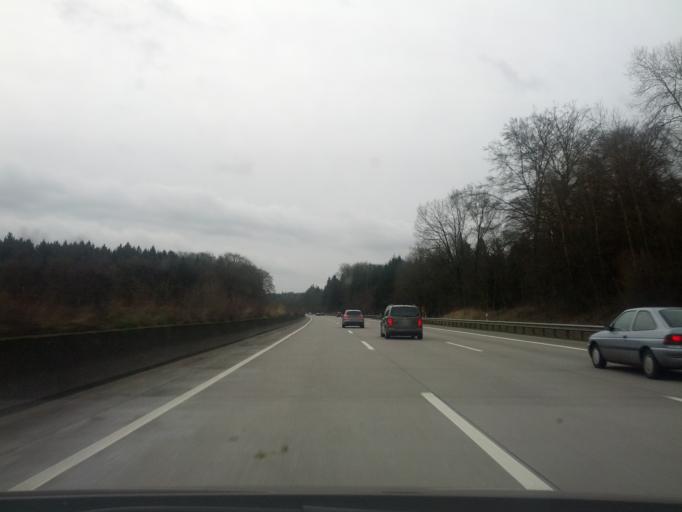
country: DE
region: Lower Saxony
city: Garlstorf
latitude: 53.2269
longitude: 10.0759
